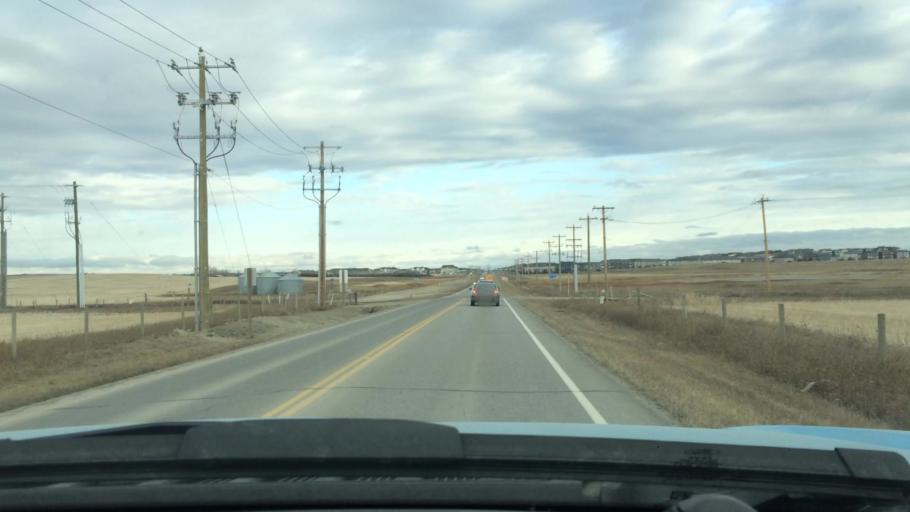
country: CA
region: Alberta
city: Airdrie
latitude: 51.2407
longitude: -114.0250
